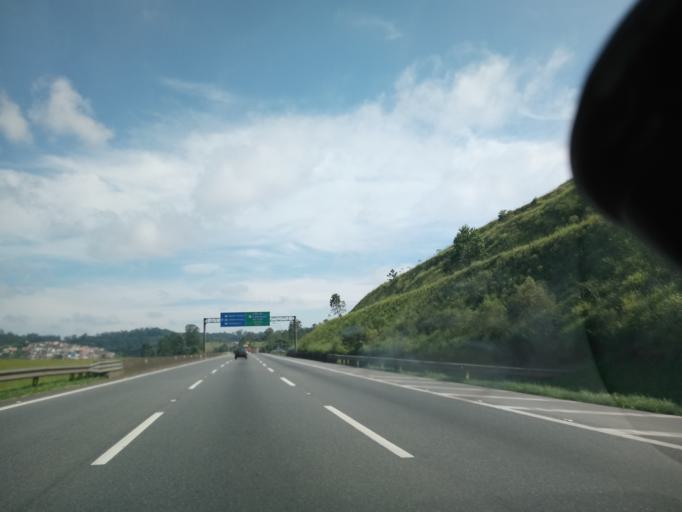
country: BR
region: Sao Paulo
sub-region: Embu
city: Embu
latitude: -23.6500
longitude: -46.8295
